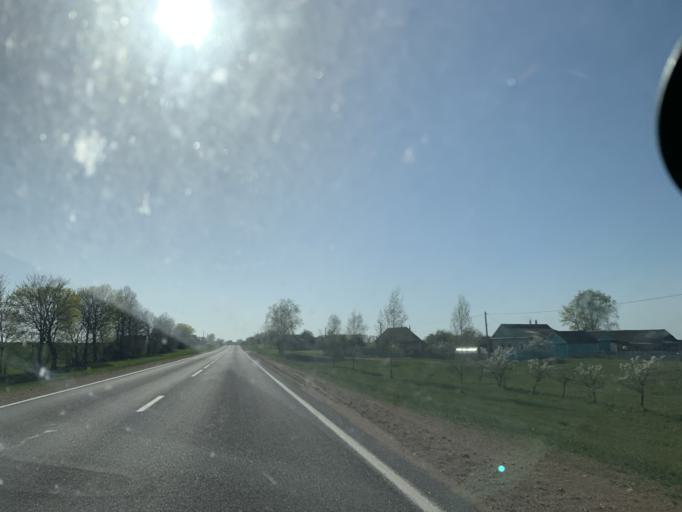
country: BY
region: Minsk
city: Nyasvizh
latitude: 53.2395
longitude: 26.8451
